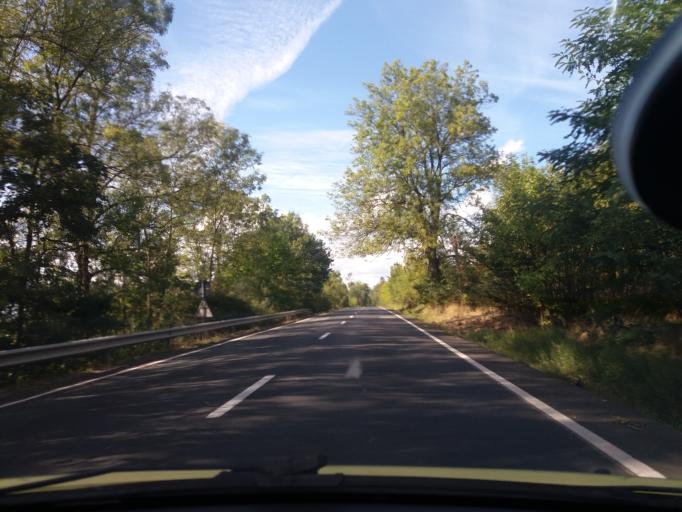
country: RO
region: Hunedoara
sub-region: Comuna Burjuc
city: Burjuc
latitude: 45.9564
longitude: 22.4837
